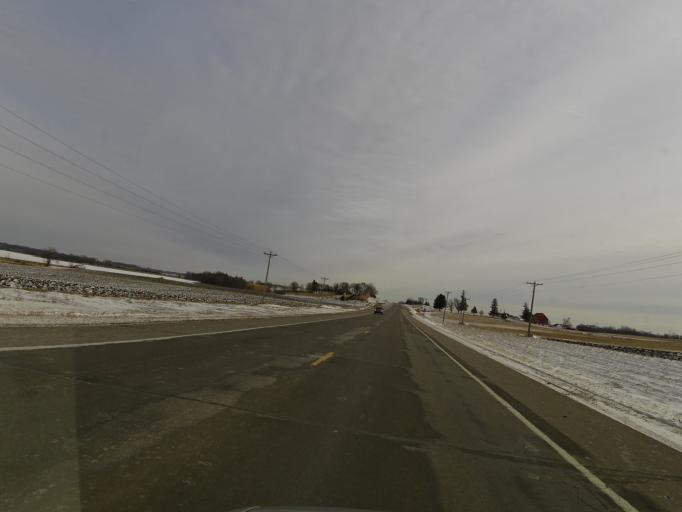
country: US
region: Minnesota
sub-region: Scott County
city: Jordan
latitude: 44.6812
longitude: -93.5577
